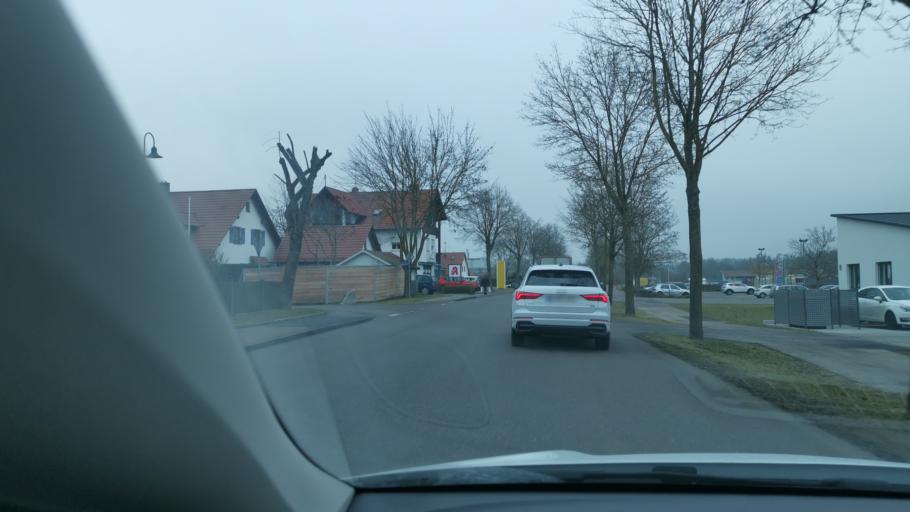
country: DE
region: Bavaria
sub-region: Swabia
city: Thierhaupten
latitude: 48.5693
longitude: 10.9069
